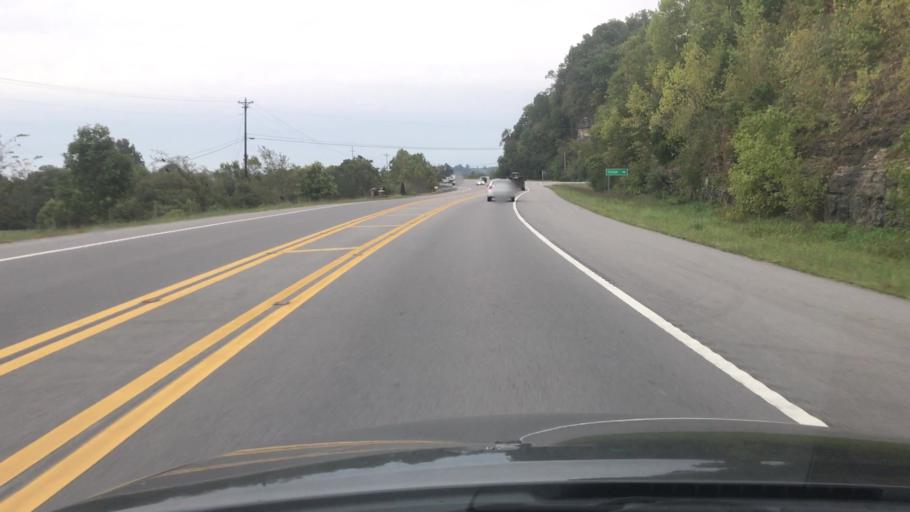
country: US
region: Tennessee
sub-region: Cheatham County
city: Ashland City
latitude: 36.2719
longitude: -87.0827
